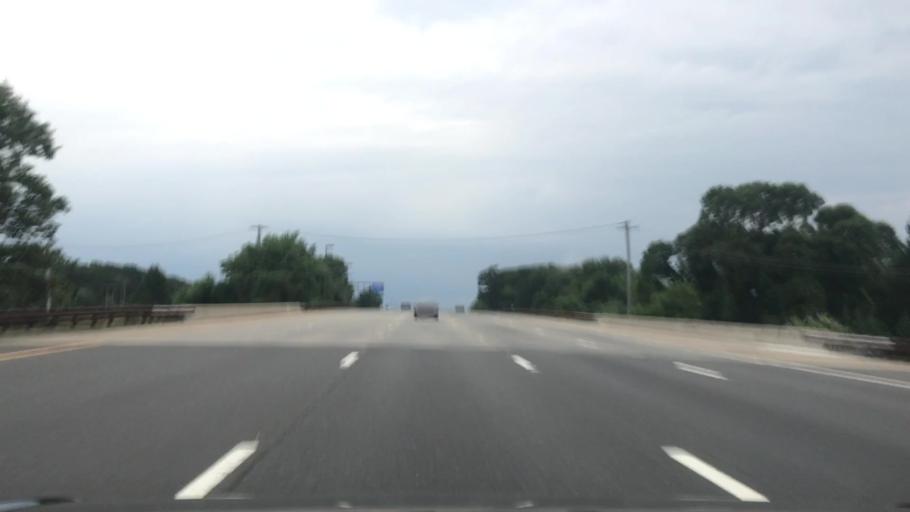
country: US
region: New Jersey
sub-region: Monmouth County
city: Shark River Hills
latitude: 40.1935
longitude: -74.0993
